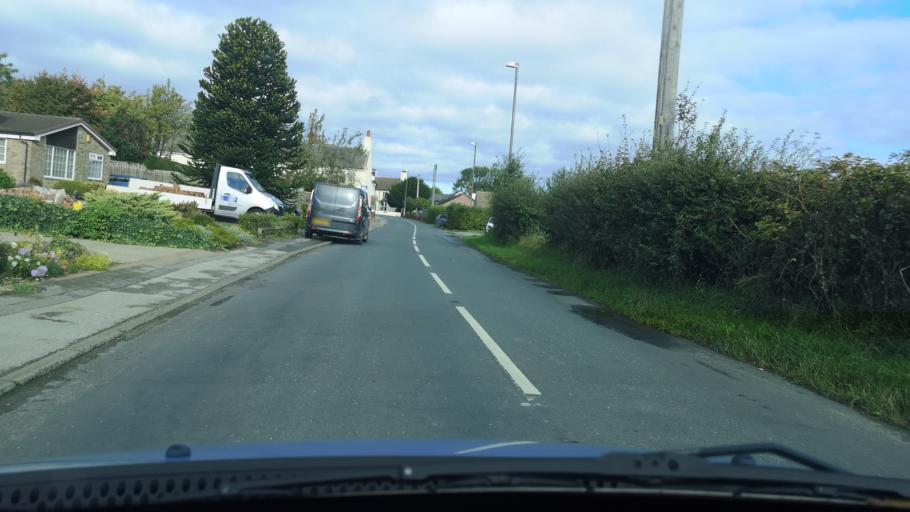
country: GB
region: England
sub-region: City and Borough of Wakefield
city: Sharlston
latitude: 53.6873
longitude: -1.3929
